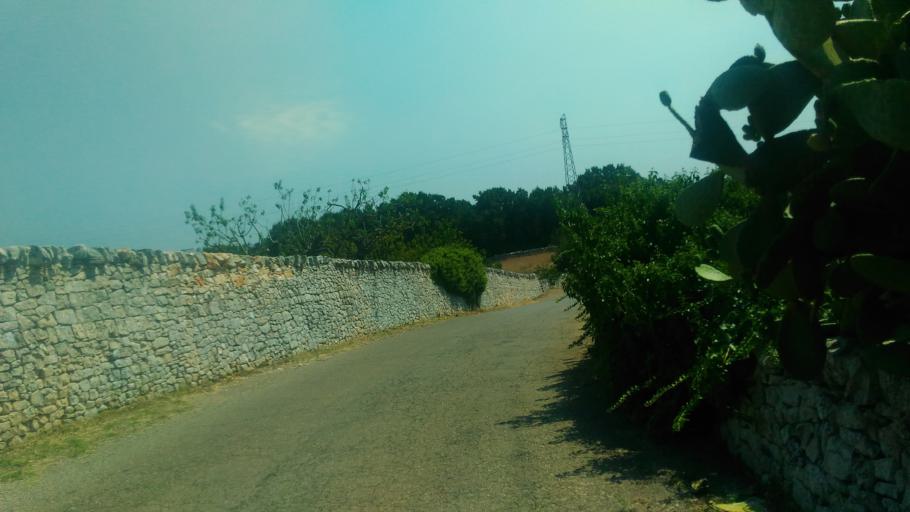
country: IT
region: Apulia
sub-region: Provincia di Brindisi
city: Cisternino
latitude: 40.7463
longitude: 17.3774
